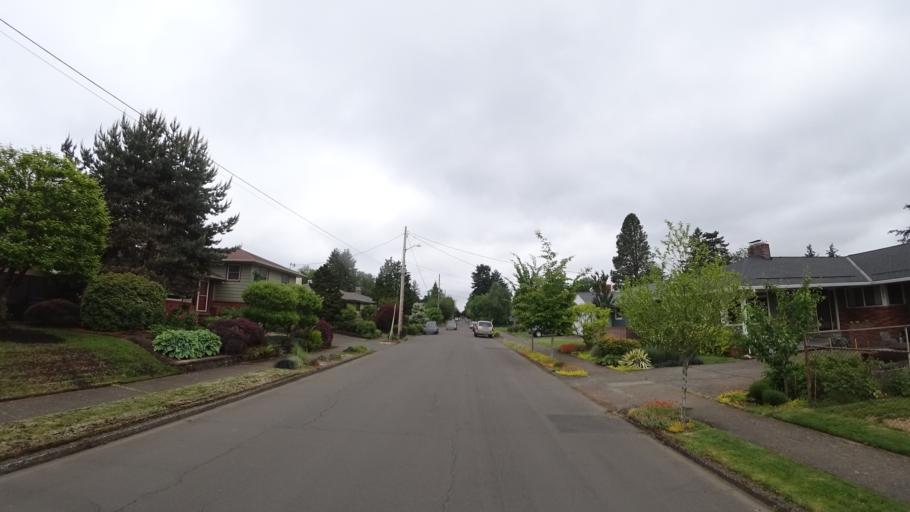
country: US
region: Oregon
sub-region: Multnomah County
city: Portland
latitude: 45.5537
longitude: -122.6126
